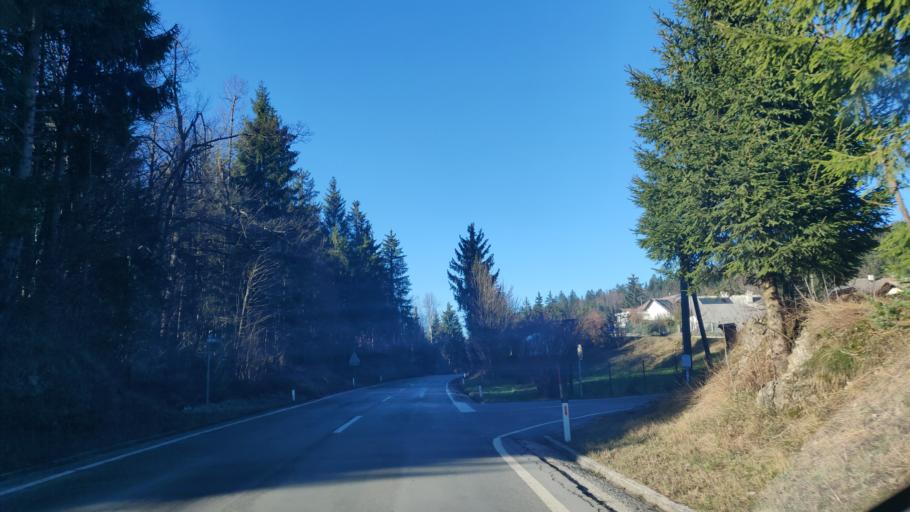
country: SI
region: Logatec
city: Logatec
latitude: 45.8764
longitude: 14.2107
